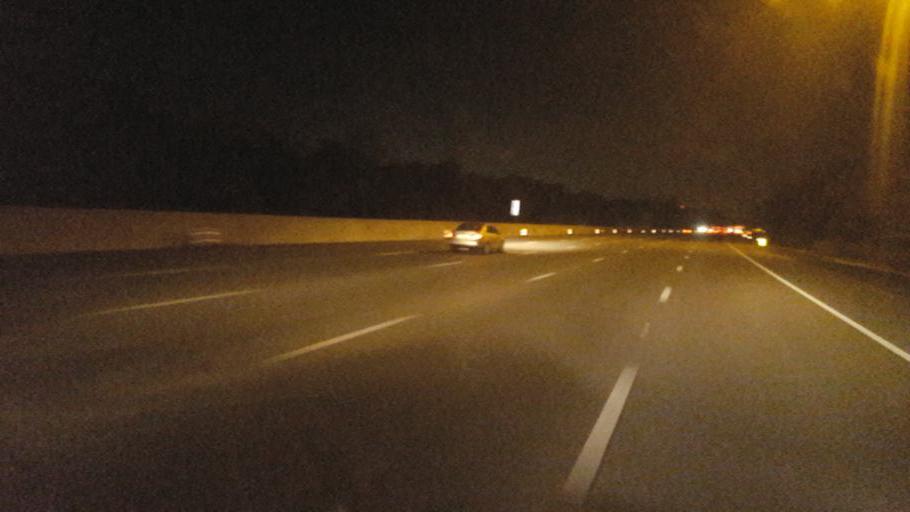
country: US
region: Ohio
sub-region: Franklin County
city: Obetz
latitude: 39.8774
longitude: -83.0110
